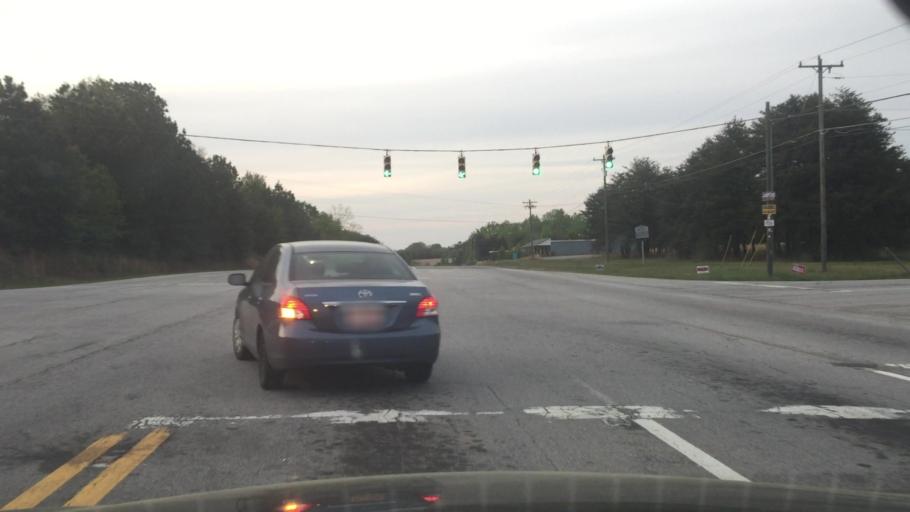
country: US
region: North Carolina
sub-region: Rockingham County
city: Reidsville
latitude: 36.3134
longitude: -79.6304
